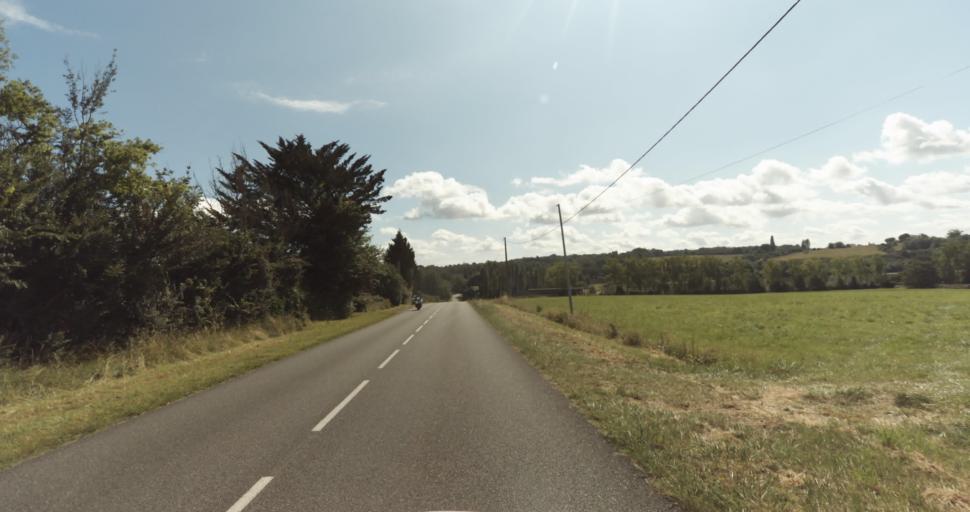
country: FR
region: Aquitaine
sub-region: Departement de la Gironde
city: Bazas
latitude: 44.4421
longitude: -0.1744
